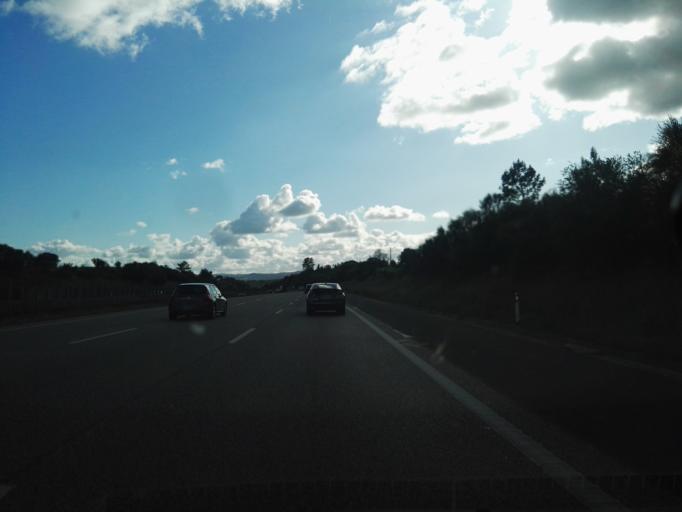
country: PT
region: Lisbon
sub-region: Azambuja
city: Aveiras de Cima
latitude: 39.1170
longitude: -8.9181
